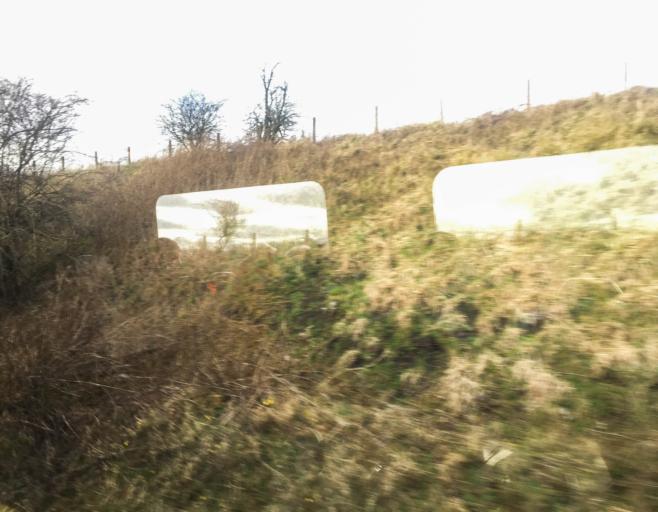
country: GB
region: Scotland
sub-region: North Lanarkshire
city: Wishaw
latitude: 55.7620
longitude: -3.9072
